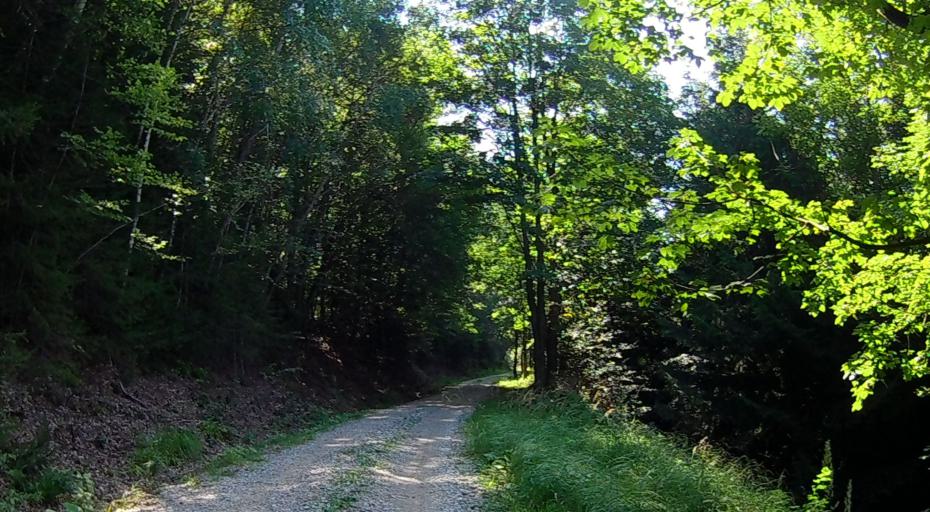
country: SI
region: Selnica ob Dravi
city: Selnica ob Dravi
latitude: 46.5051
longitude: 15.4664
